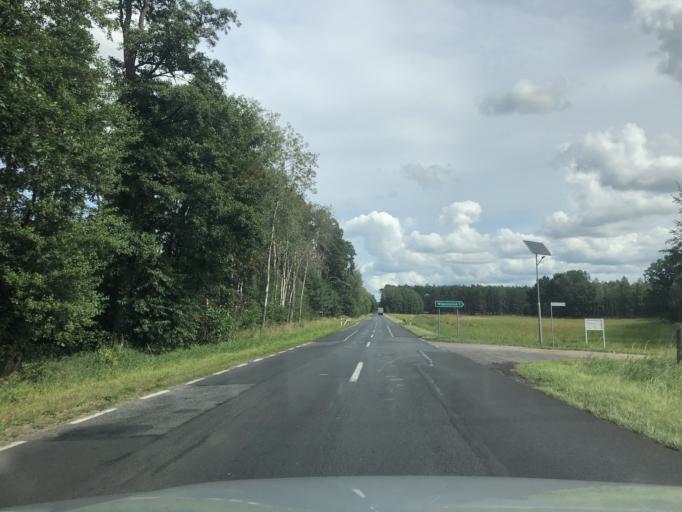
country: PL
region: Greater Poland Voivodeship
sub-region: Powiat czarnkowsko-trzcianecki
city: Trzcianka
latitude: 53.0694
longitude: 16.5585
